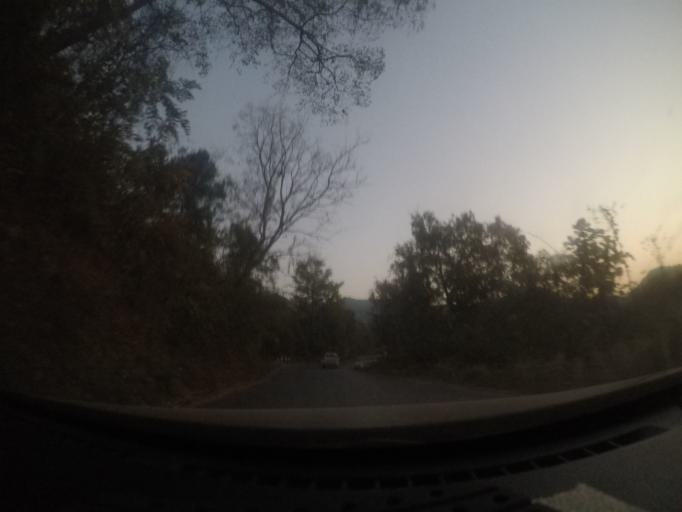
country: MM
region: Mandalay
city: Yamethin
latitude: 20.6948
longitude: 96.5059
